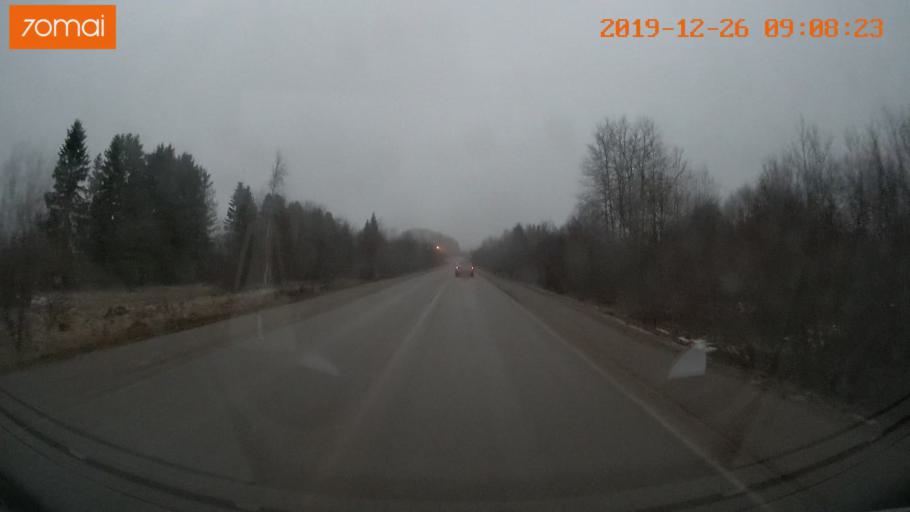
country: RU
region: Vologda
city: Gryazovets
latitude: 58.8562
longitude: 40.2481
